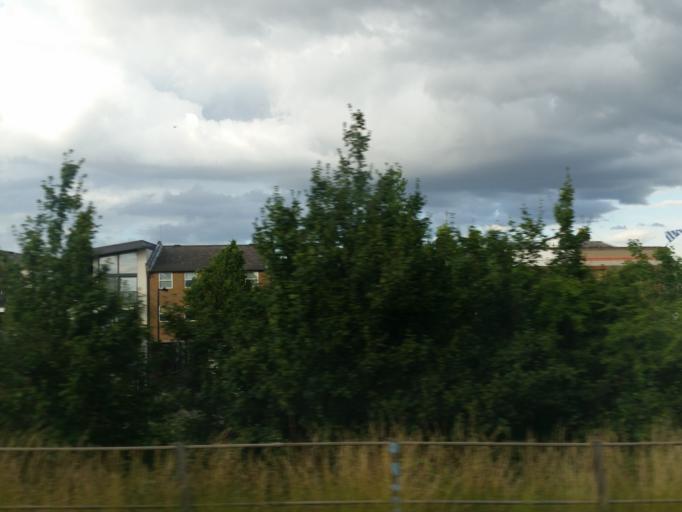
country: GB
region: England
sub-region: Greater London
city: Hammersmith
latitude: 51.5180
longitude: -0.2251
